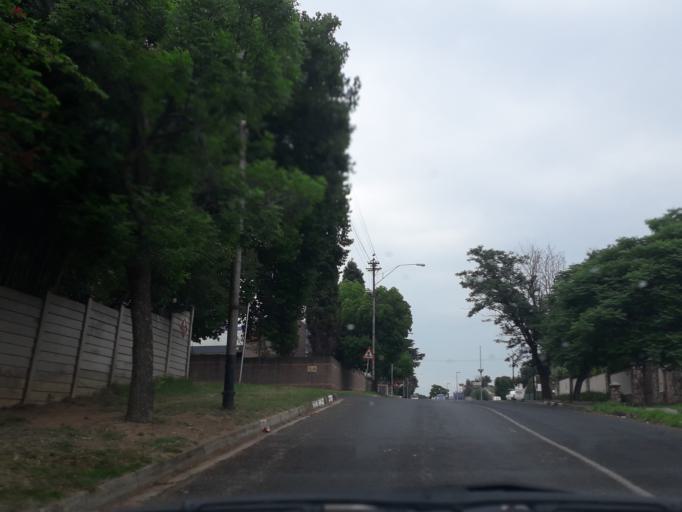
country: ZA
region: Gauteng
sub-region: City of Johannesburg Metropolitan Municipality
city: Johannesburg
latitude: -26.1446
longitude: 28.0974
